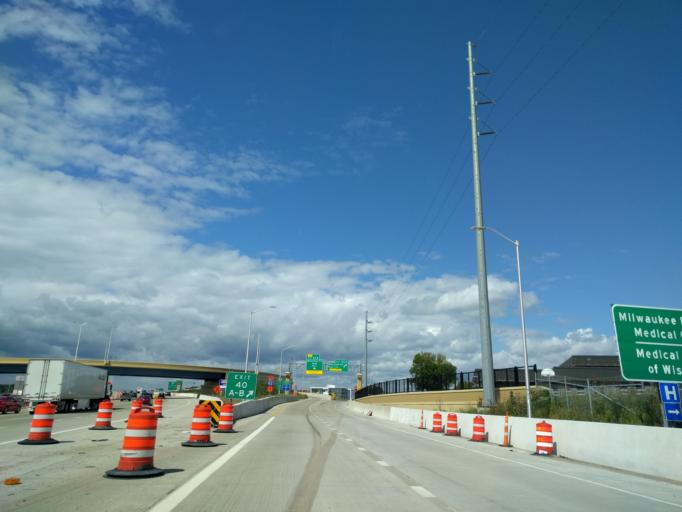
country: US
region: Wisconsin
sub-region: Milwaukee County
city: Wauwatosa
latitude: 43.0423
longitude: -88.0332
